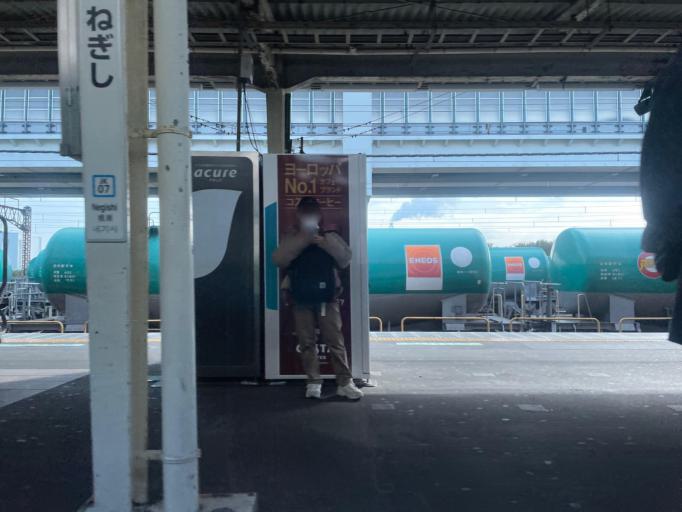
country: JP
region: Kanagawa
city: Yokohama
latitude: 35.4159
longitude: 139.6365
